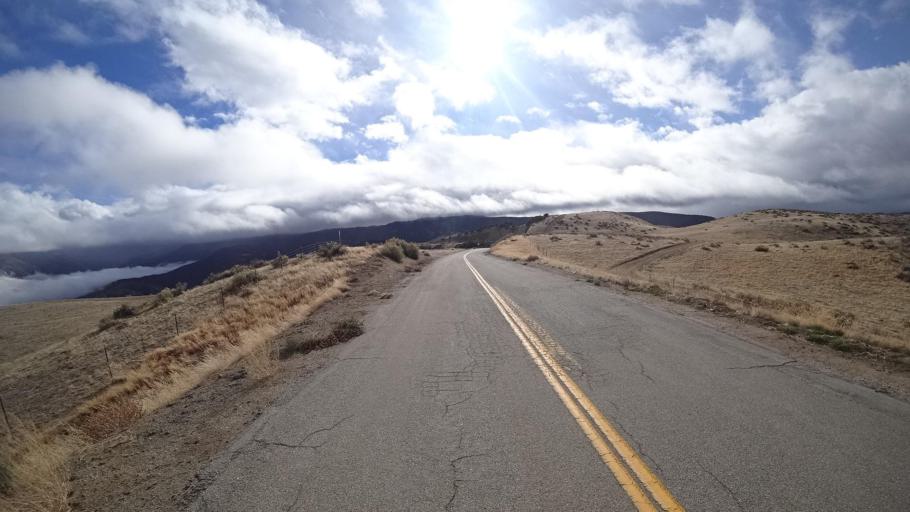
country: US
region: California
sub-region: Kern County
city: Maricopa
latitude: 34.8994
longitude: -119.3666
